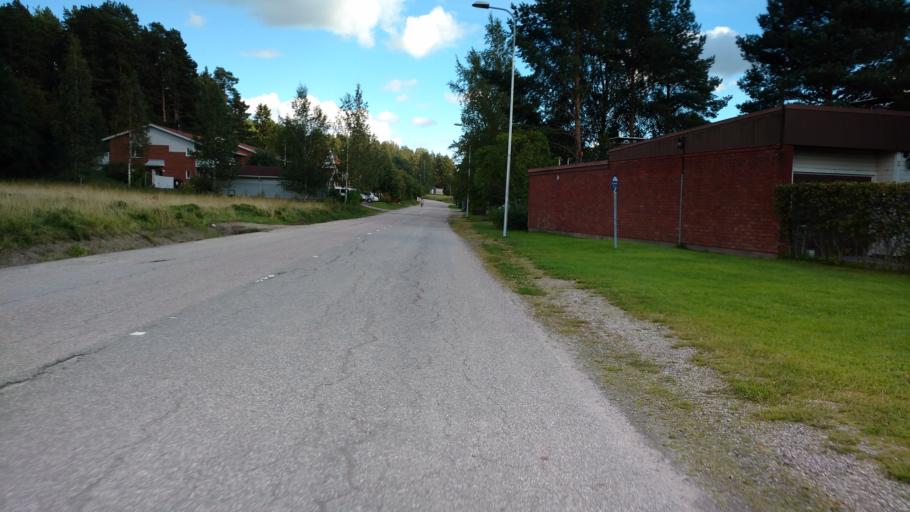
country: FI
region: Varsinais-Suomi
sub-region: Salo
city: Salo
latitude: 60.3803
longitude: 23.1624
